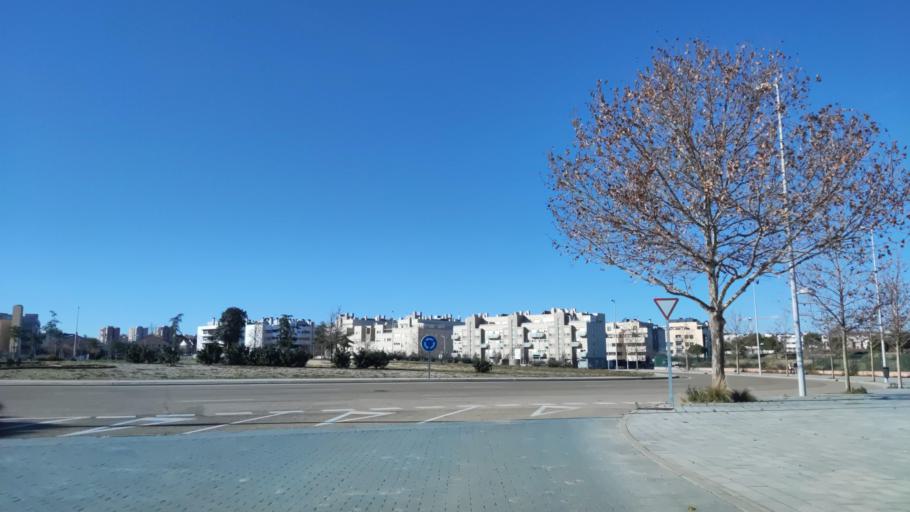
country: ES
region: Madrid
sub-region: Provincia de Madrid
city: Hortaleza
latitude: 40.4826
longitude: -3.6249
